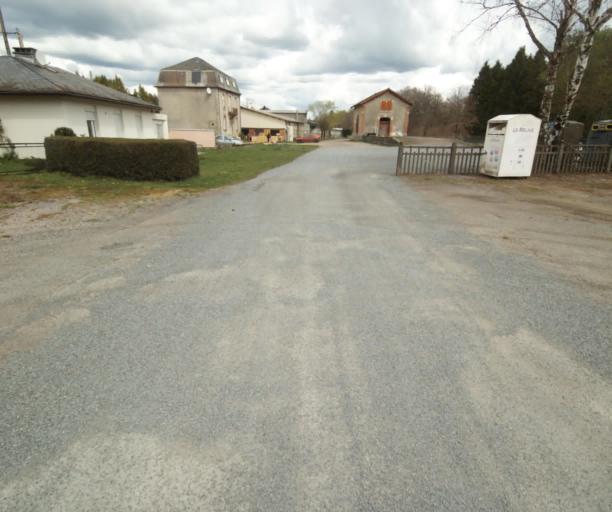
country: FR
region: Limousin
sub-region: Departement de la Correze
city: Correze
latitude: 45.3412
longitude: 1.9314
